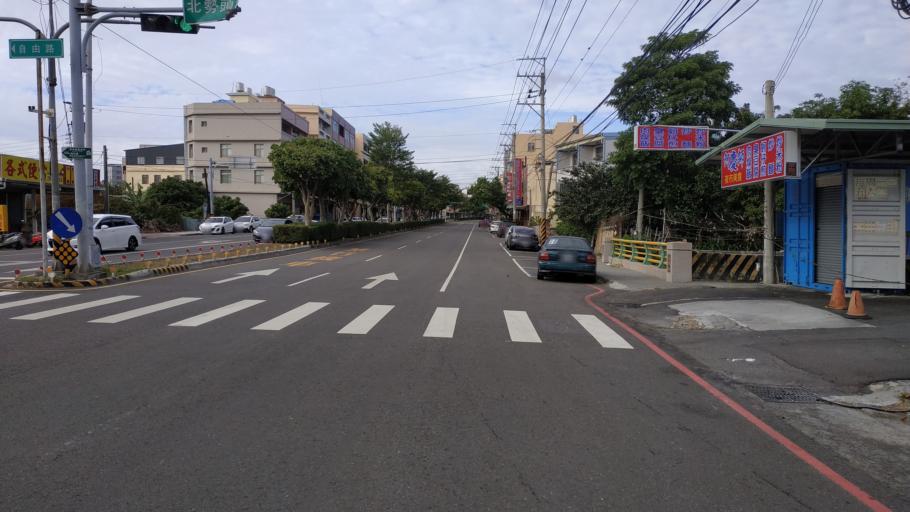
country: TW
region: Taiwan
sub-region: Taichung City
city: Taichung
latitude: 24.2205
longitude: 120.5695
